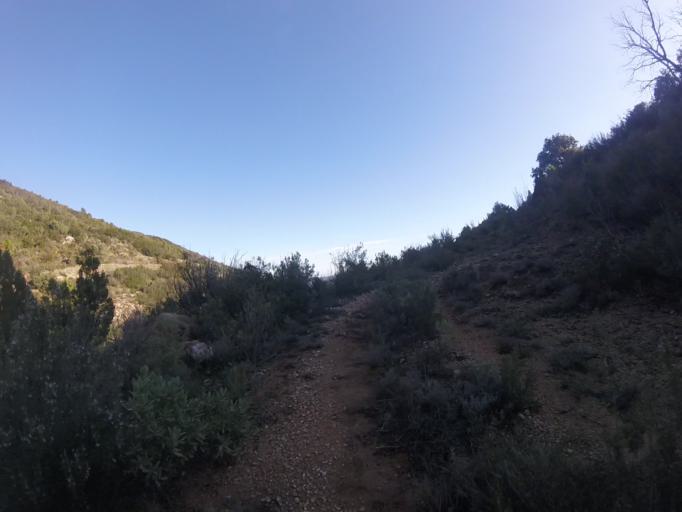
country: ES
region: Valencia
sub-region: Provincia de Castello
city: Sarratella
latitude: 40.2930
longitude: 0.0503
